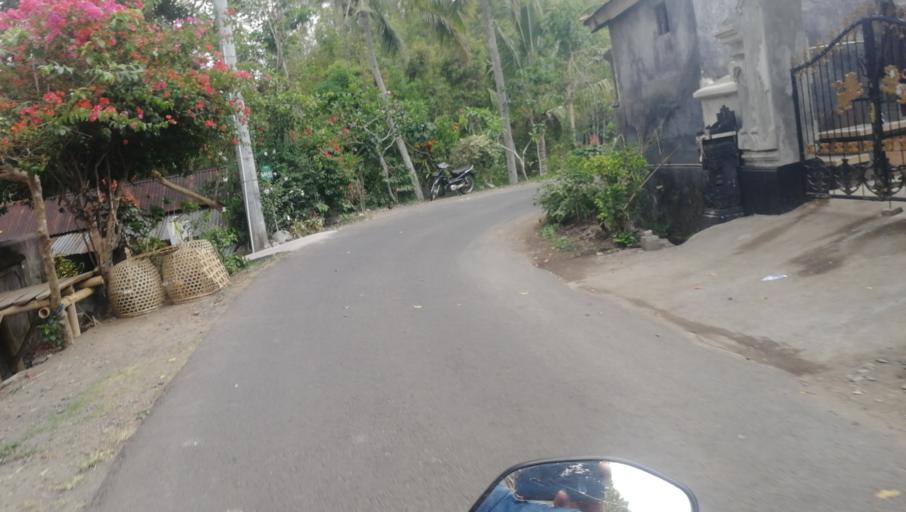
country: ID
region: Bali
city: Munduk
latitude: -8.2818
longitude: 115.0375
